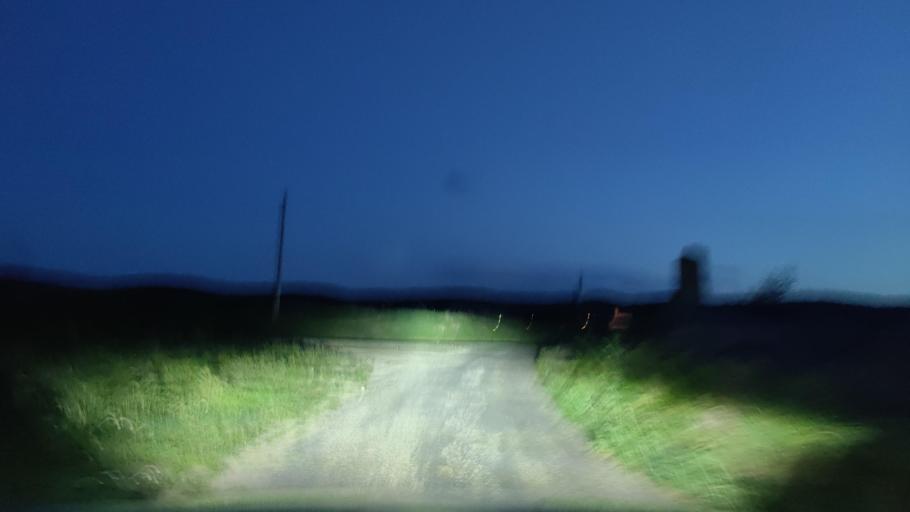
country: FR
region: Languedoc-Roussillon
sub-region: Departement des Pyrenees-Orientales
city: Estagel
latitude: 42.8647
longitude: 2.7248
